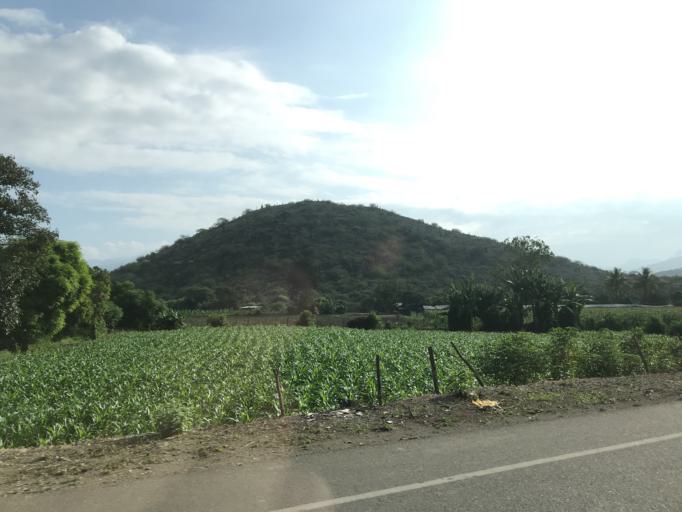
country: PE
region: Lambayeque
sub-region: Provincia de Chiclayo
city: Chongoyape
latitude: -6.6327
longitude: -79.3928
